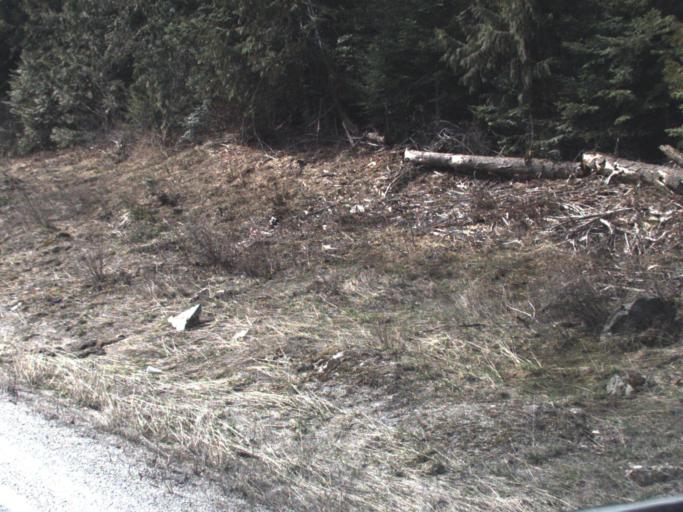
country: US
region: Washington
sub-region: Stevens County
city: Chewelah
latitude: 48.5745
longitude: -117.3523
